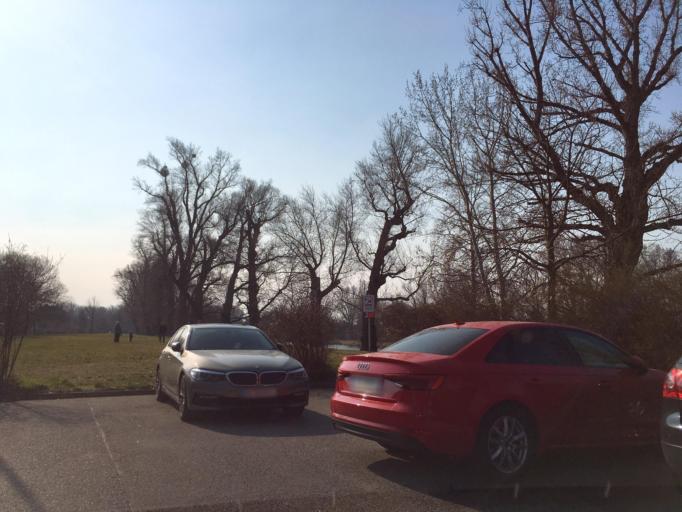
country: AT
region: Lower Austria
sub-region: Politischer Bezirk Wien-Umgebung
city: Schwechat
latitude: 48.2087
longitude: 16.4746
